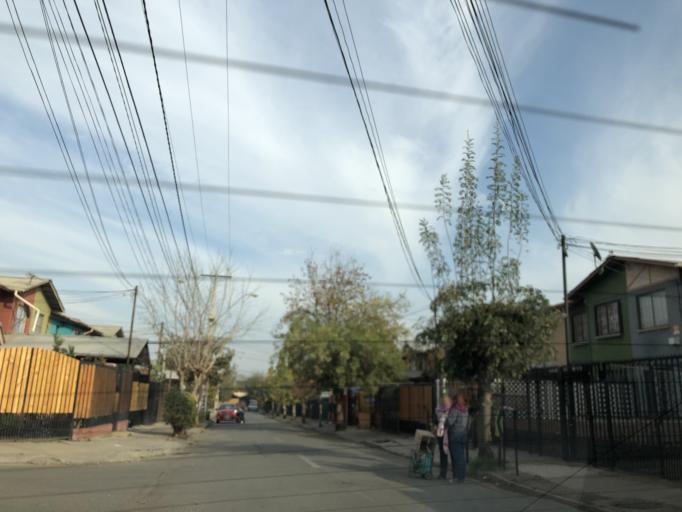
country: CL
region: Santiago Metropolitan
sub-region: Provincia de Cordillera
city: Puente Alto
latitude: -33.5809
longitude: -70.5533
